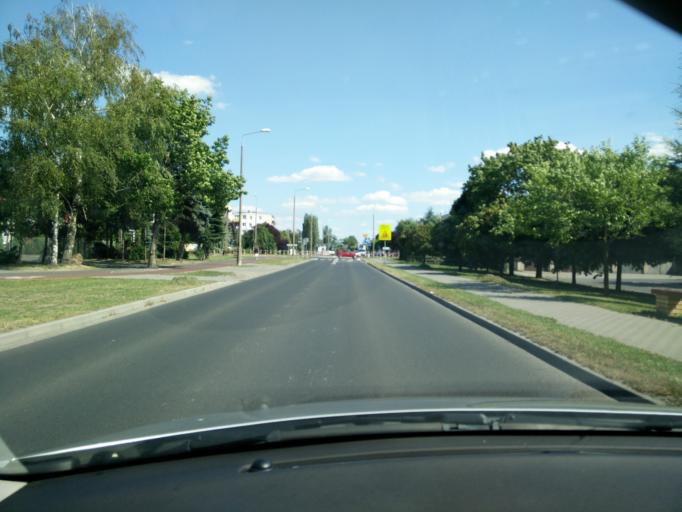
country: PL
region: Greater Poland Voivodeship
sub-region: Powiat sredzki
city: Sroda Wielkopolska
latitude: 52.2264
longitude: 17.2684
